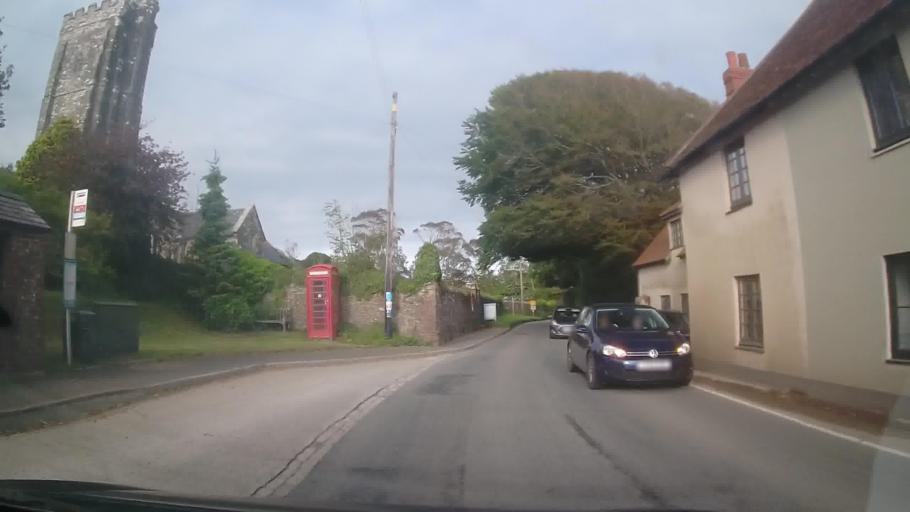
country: GB
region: England
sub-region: Devon
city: Kingsbridge
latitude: 50.2989
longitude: -3.8100
